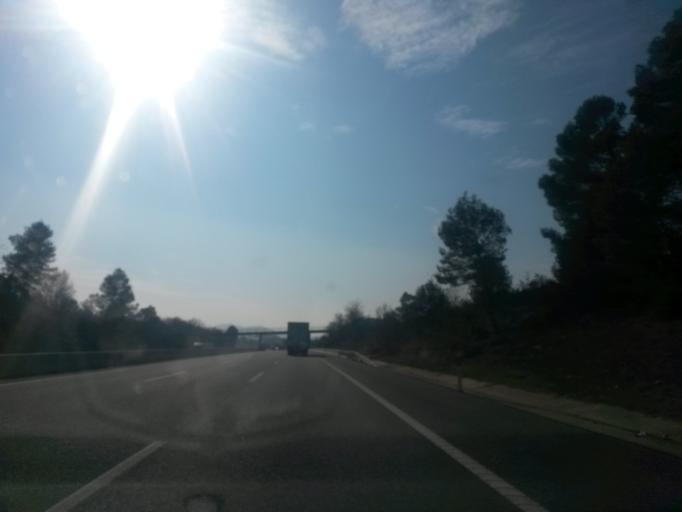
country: ES
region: Catalonia
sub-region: Provincia de Girona
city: Cervia de Ter
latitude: 42.0905
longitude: 2.8923
